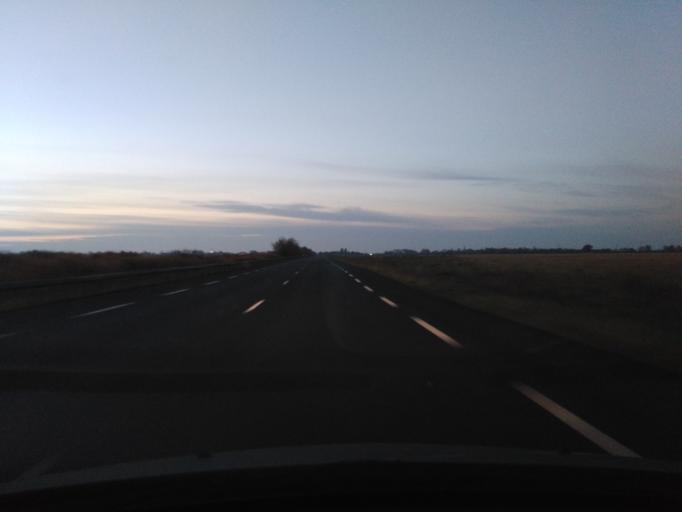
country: FR
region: Pays de la Loire
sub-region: Departement de la Vendee
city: Champagne-les-Marais
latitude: 46.3889
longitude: -1.0935
